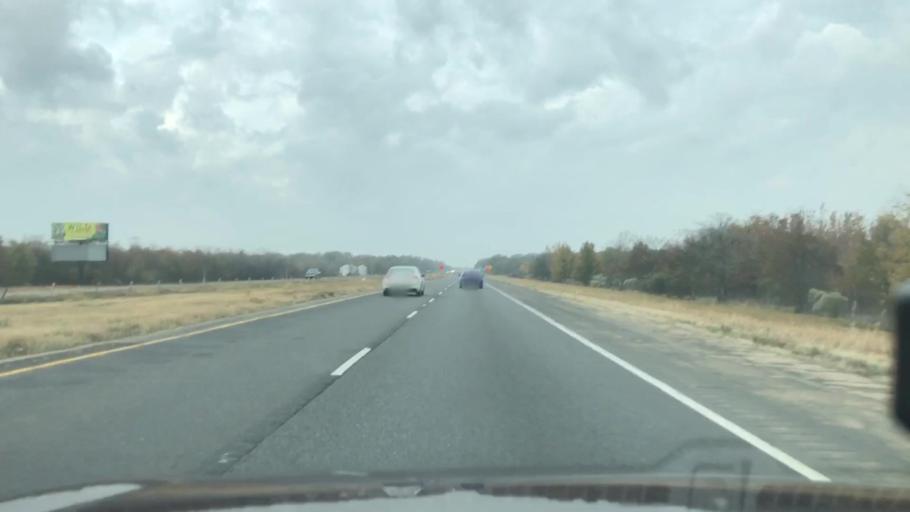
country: US
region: Louisiana
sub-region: Richland Parish
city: Delhi
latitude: 32.4382
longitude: -91.4633
